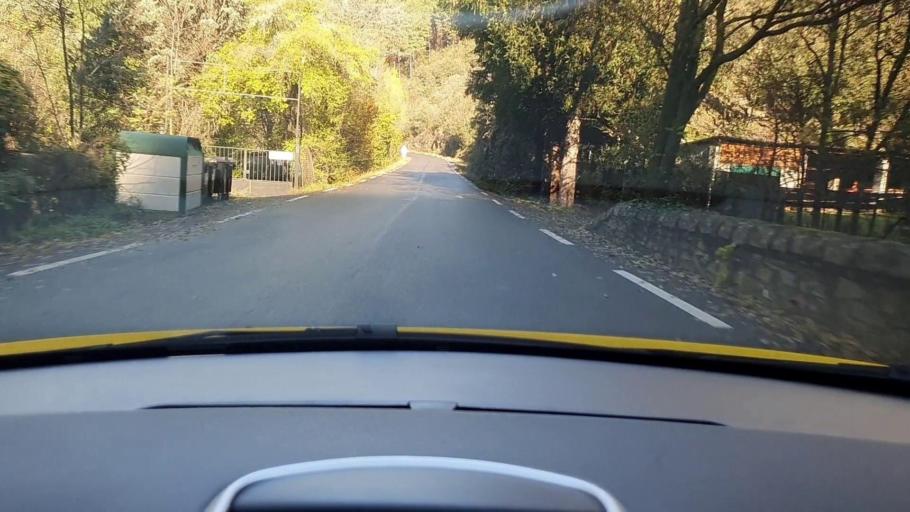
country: FR
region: Languedoc-Roussillon
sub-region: Departement du Gard
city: Valleraugue
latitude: 44.1356
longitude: 3.7579
